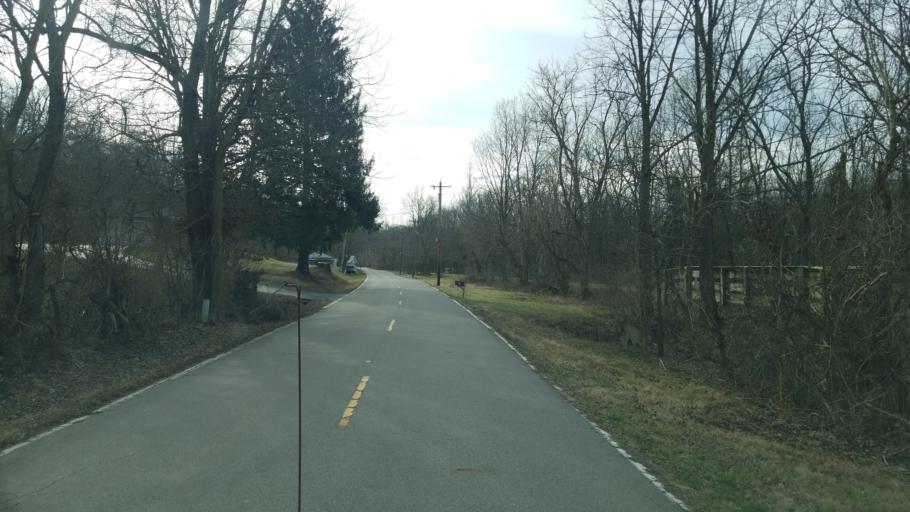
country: US
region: Ohio
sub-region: Warren County
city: Waynesville
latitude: 39.4411
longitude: -84.1009
